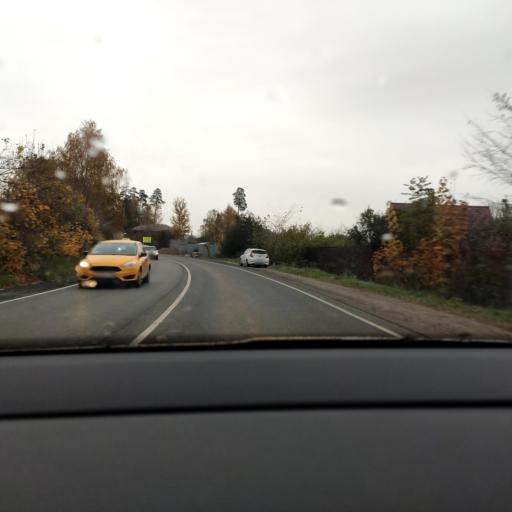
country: RU
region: Moskovskaya
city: Lesnyye Polyany
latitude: 55.9700
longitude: 37.8716
